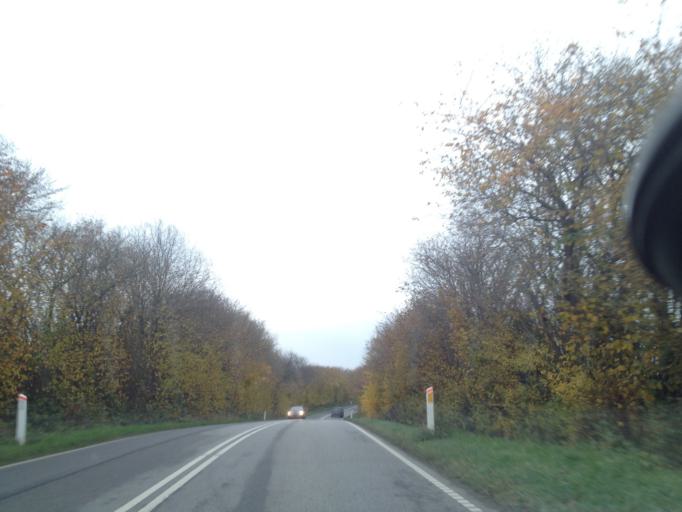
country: DK
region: South Denmark
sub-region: Assens Kommune
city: Vissenbjerg
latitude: 55.4480
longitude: 10.1296
